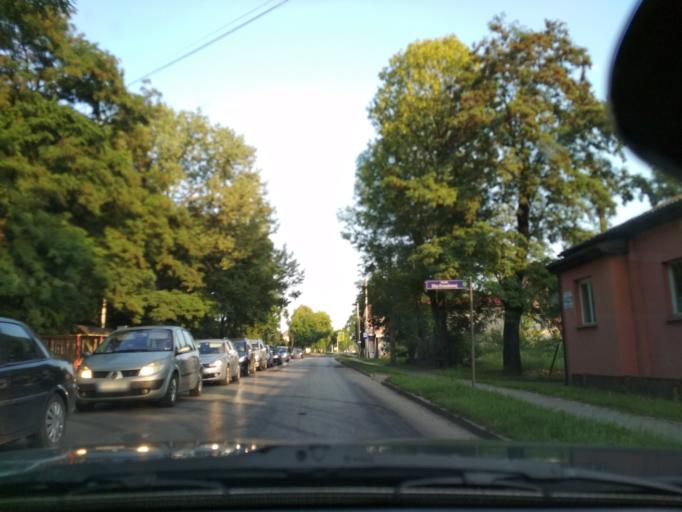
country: PL
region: Silesian Voivodeship
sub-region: Powiat zawiercianski
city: Ogrodzieniec
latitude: 50.4625
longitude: 19.4945
